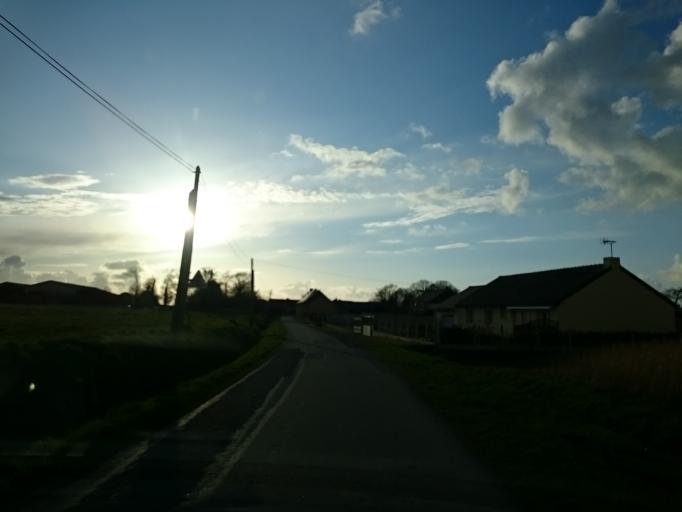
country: FR
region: Brittany
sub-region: Departement d'Ille-et-Vilaine
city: Crevin
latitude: 47.9200
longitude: -1.6424
